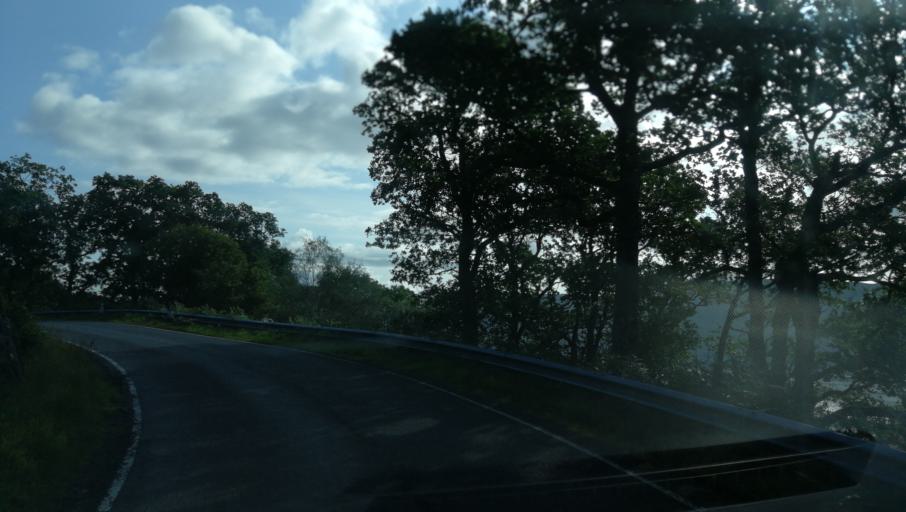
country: GB
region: Scotland
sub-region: Argyll and Bute
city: Isle Of Mull
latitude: 56.6808
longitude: -5.8288
